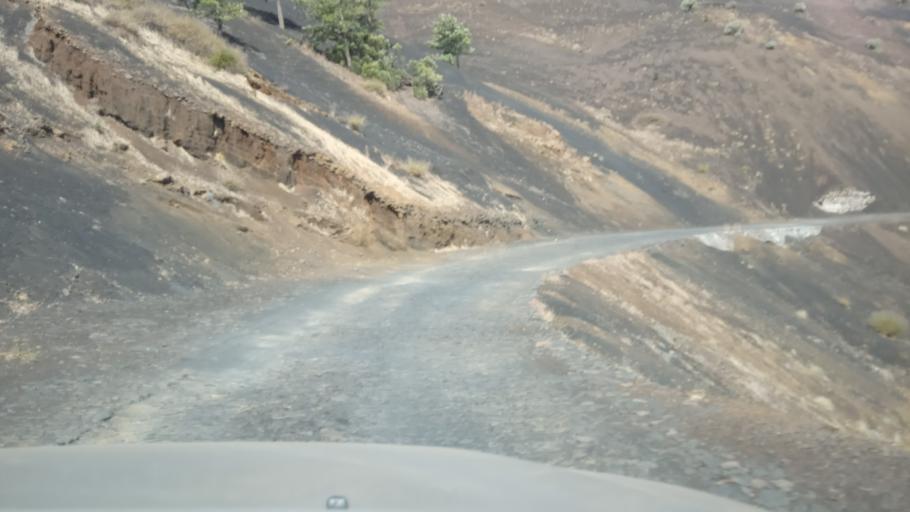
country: CV
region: Santa Catarina do Fogo
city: Cova Figueira
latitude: 14.9163
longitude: -24.3429
